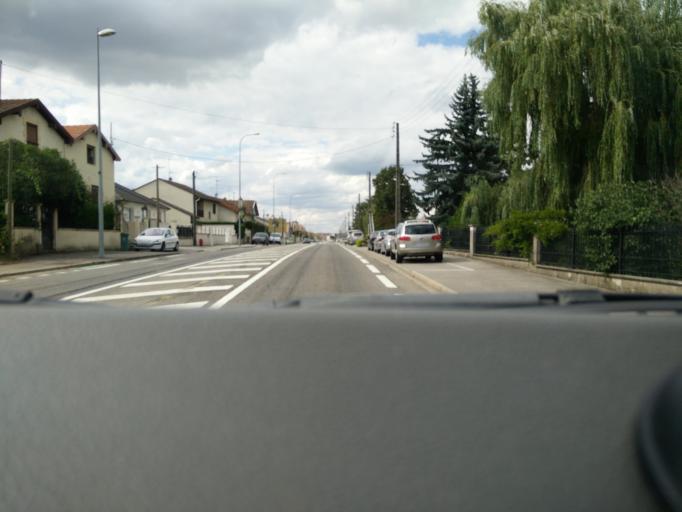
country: FR
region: Lorraine
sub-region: Departement de Meurthe-et-Moselle
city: Laneuveville-devant-Nancy
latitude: 48.6485
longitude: 6.2408
